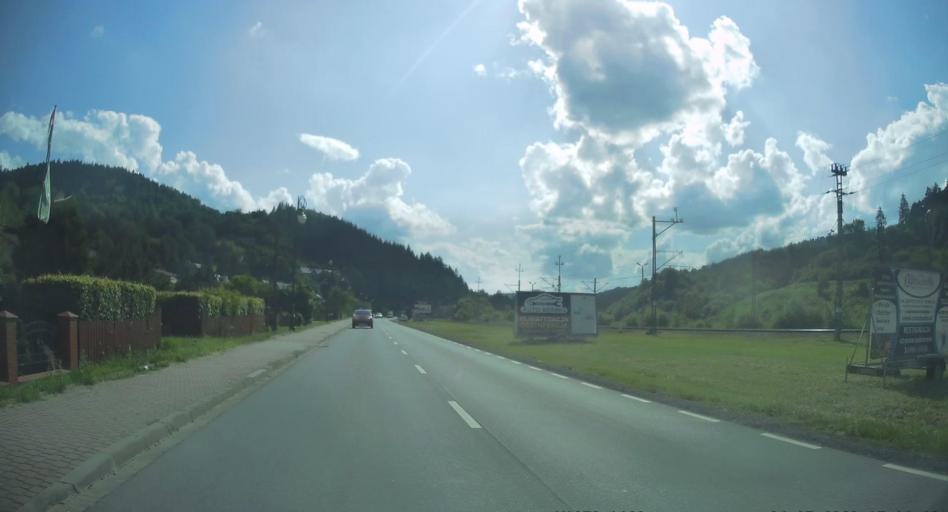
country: PL
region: Lesser Poland Voivodeship
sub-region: Powiat nowosadecki
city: Muszyna
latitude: 49.3663
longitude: 20.9363
